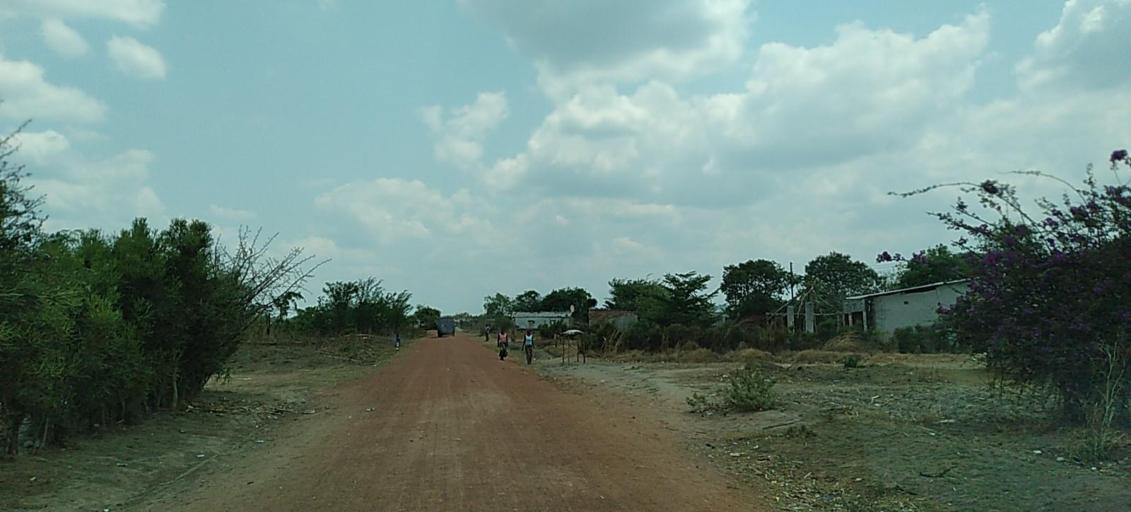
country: ZM
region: Copperbelt
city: Luanshya
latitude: -13.1250
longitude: 28.3103
